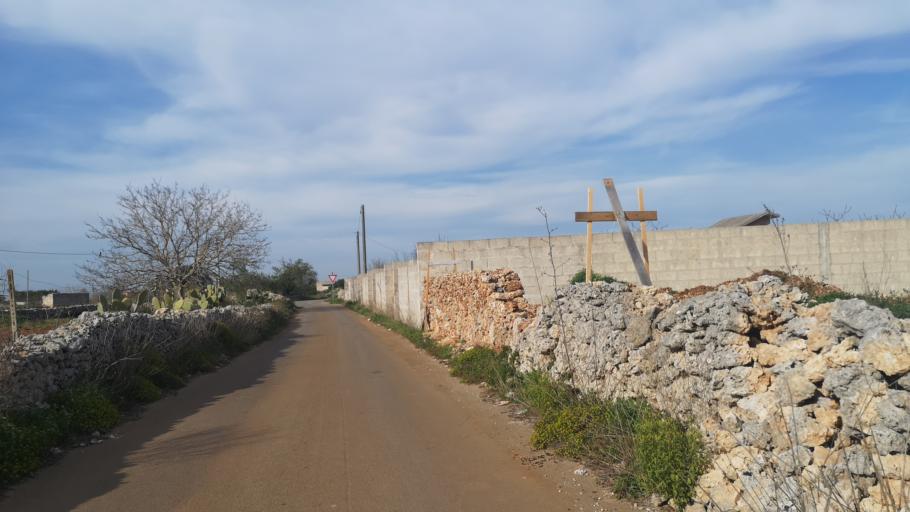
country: IT
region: Apulia
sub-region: Provincia di Lecce
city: Spongano
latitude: 40.0226
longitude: 18.3703
